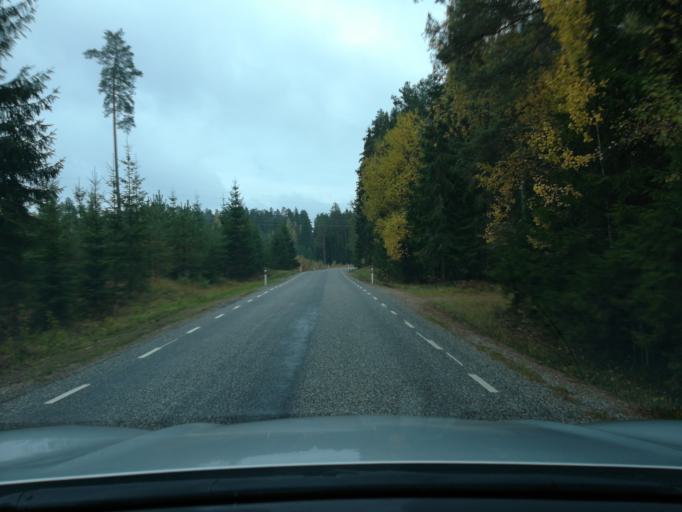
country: EE
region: Ida-Virumaa
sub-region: Johvi vald
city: Johvi
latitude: 59.1786
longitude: 27.4576
